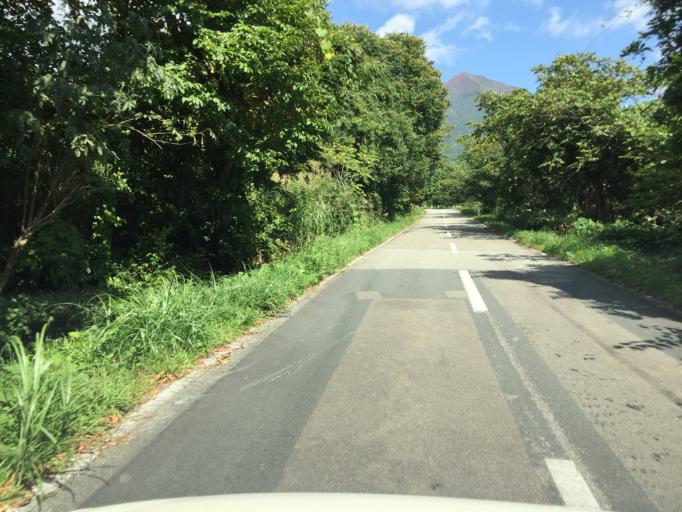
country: JP
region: Fukushima
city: Inawashiro
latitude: 37.5858
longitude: 140.0285
